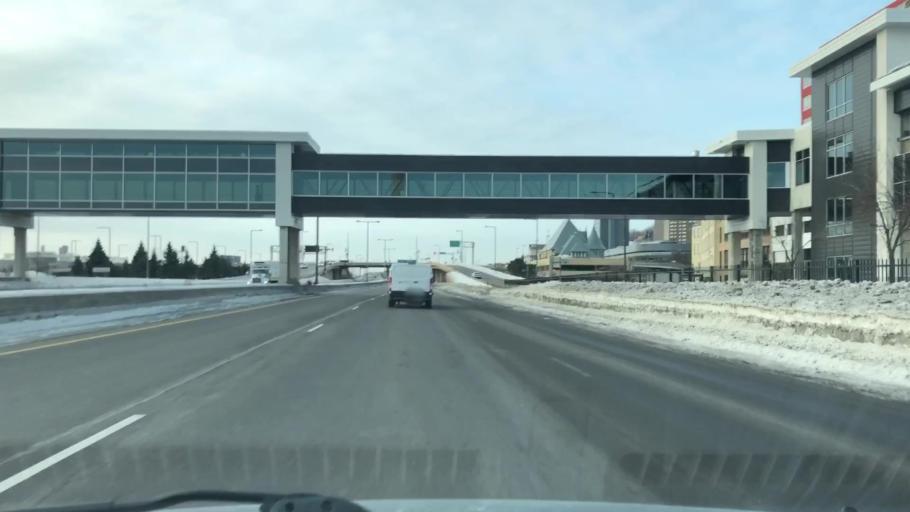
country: US
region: Minnesota
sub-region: Saint Louis County
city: Duluth
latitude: 46.7836
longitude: -92.1000
